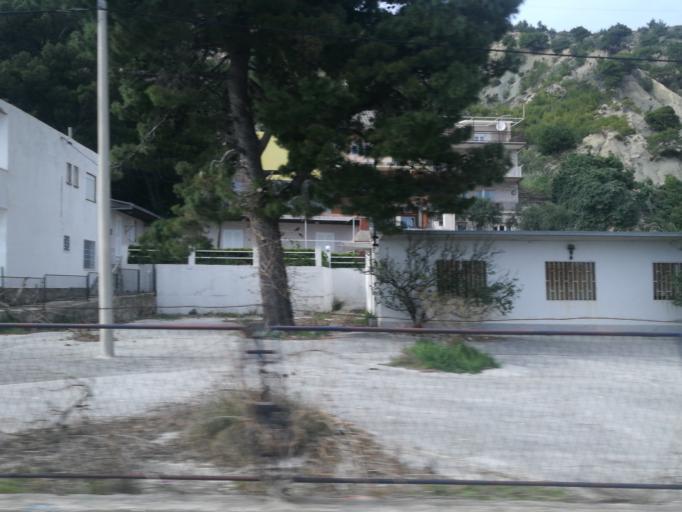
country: HR
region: Splitsko-Dalmatinska
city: Duce
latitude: 43.4417
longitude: 16.6508
